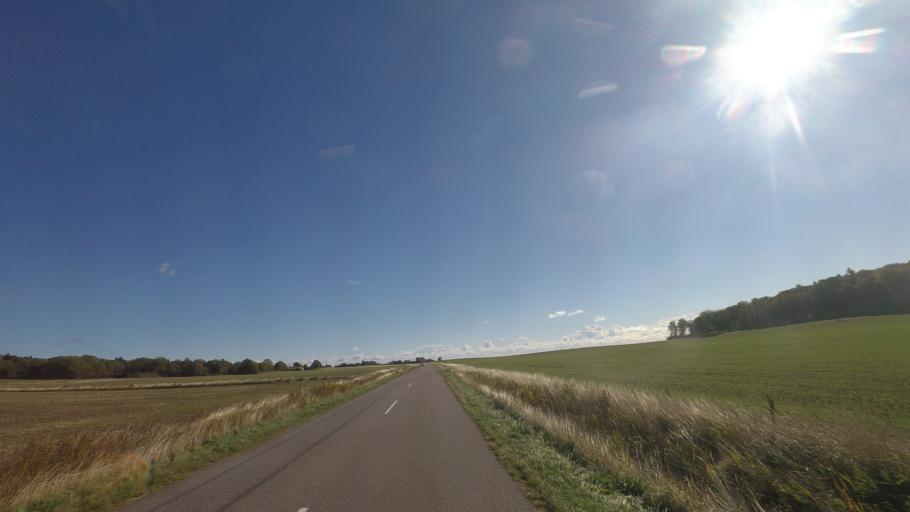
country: DK
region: Capital Region
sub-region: Bornholm Kommune
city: Nexo
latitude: 55.0777
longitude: 15.0832
